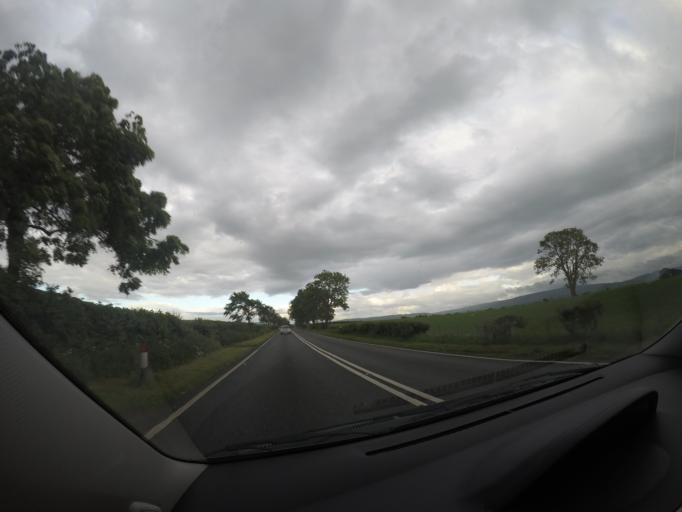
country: GB
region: England
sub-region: Cumbria
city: Kirkby Stephen
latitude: 54.5319
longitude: -2.3437
